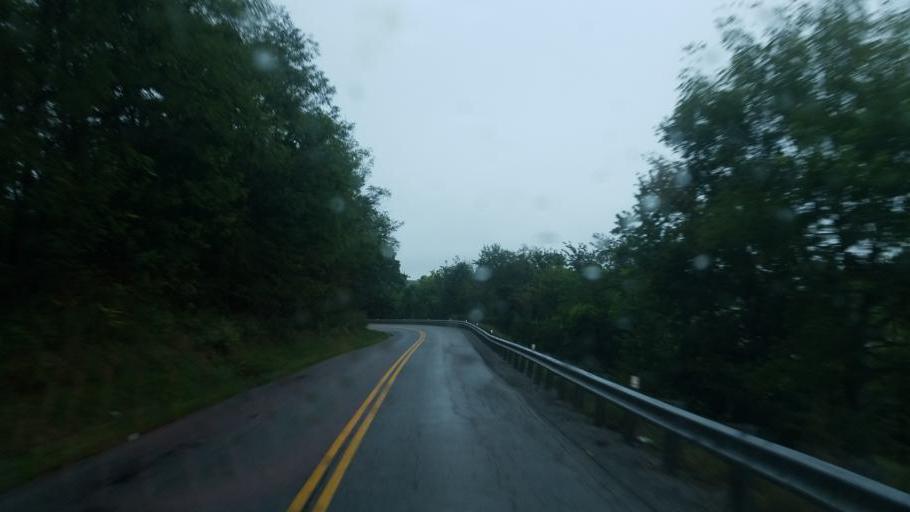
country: US
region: Kentucky
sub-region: Fleming County
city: Flemingsburg
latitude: 38.4143
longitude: -83.6902
